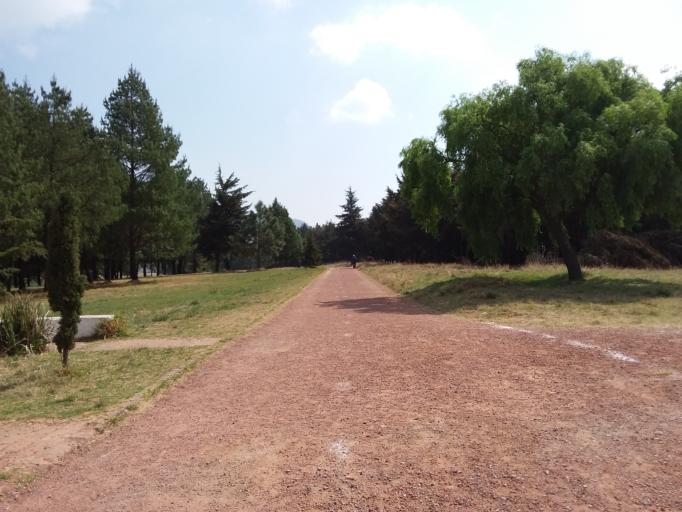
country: MX
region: Mexico
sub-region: Toluca
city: San Antonio Buenavista
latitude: 19.2726
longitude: -99.6982
